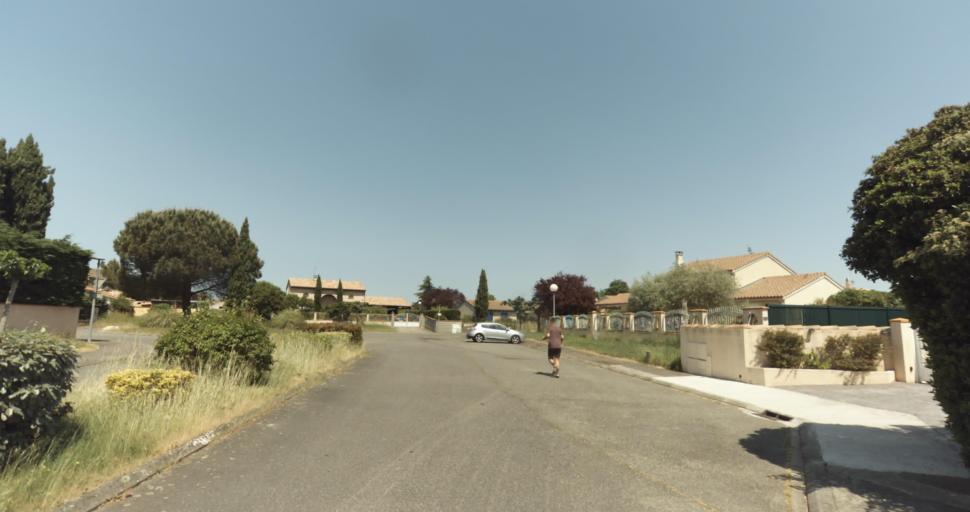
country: FR
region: Midi-Pyrenees
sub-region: Departement de la Haute-Garonne
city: La Salvetat-Saint-Gilles
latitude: 43.5651
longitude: 1.2700
